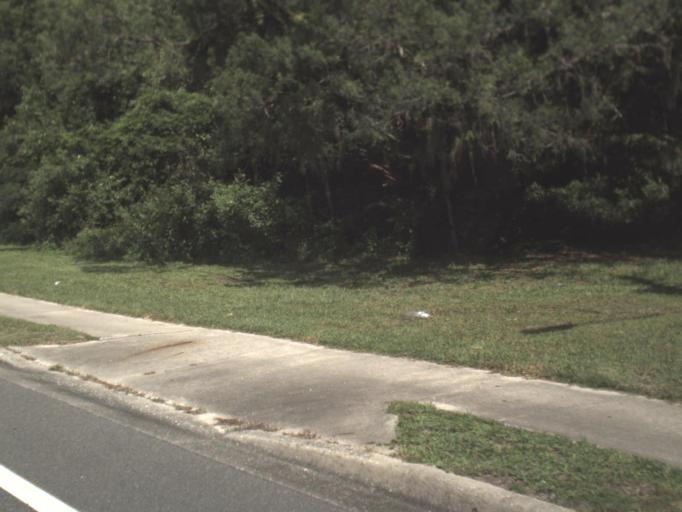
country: US
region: Florida
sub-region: Alachua County
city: Gainesville
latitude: 29.6029
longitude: -82.4139
